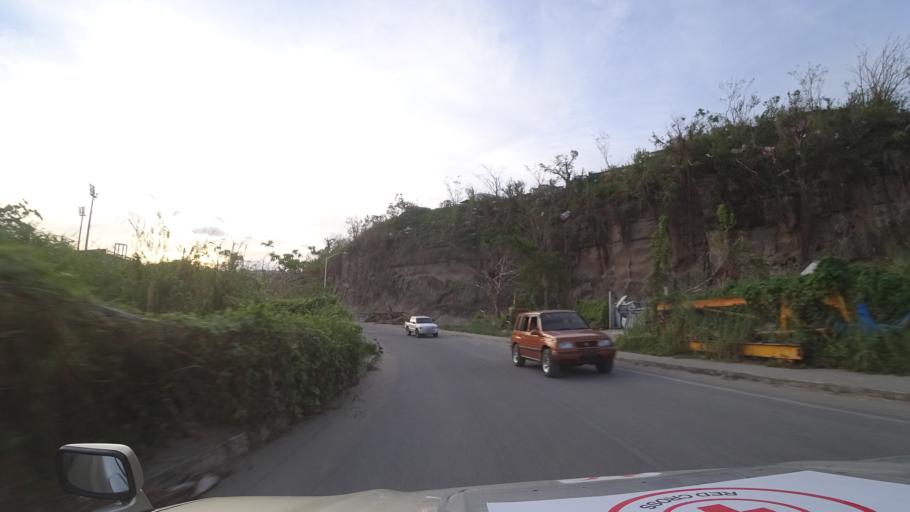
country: DM
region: Saint George
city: Roseau
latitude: 15.3033
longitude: -61.3826
